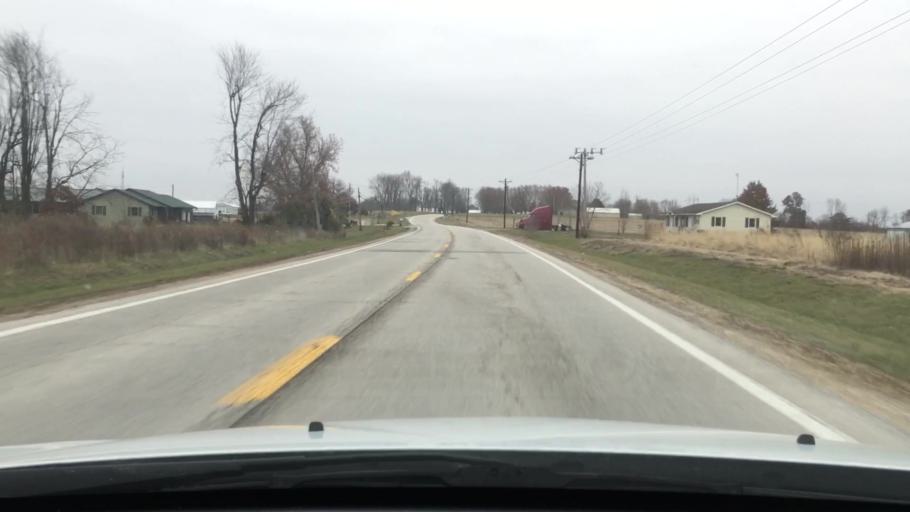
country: US
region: Illinois
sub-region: Pike County
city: Pittsfield
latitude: 39.5689
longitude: -90.9140
